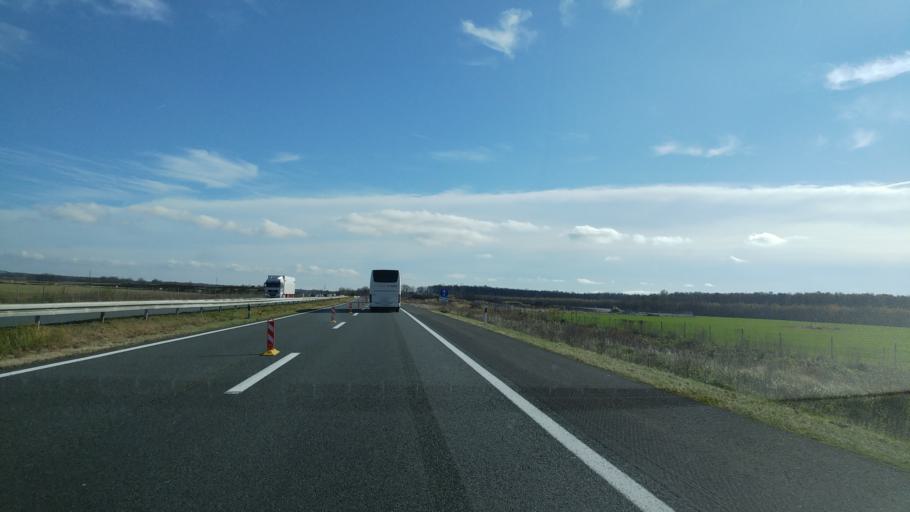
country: HR
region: Sisacko-Moslavacka
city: Lipovljani
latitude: 45.3754
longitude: 16.8789
